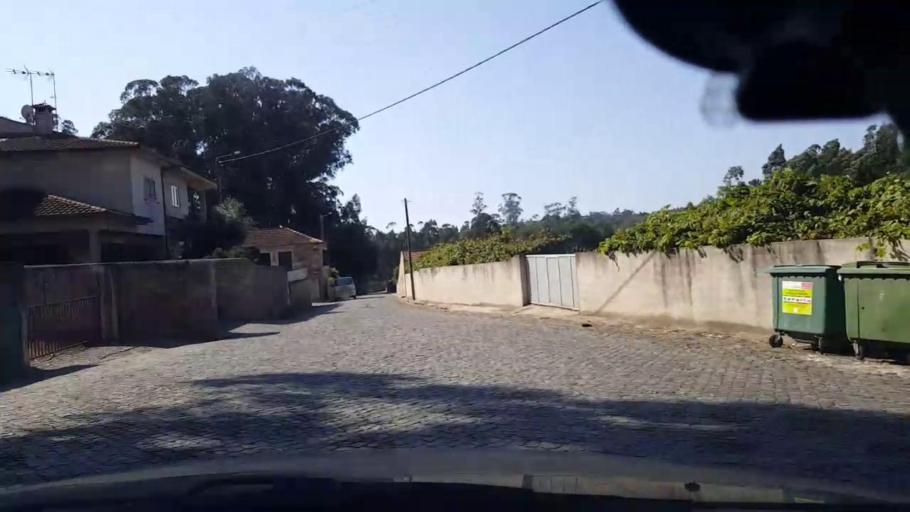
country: PT
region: Porto
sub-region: Povoa de Varzim
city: Pedroso
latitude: 41.4037
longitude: -8.7069
